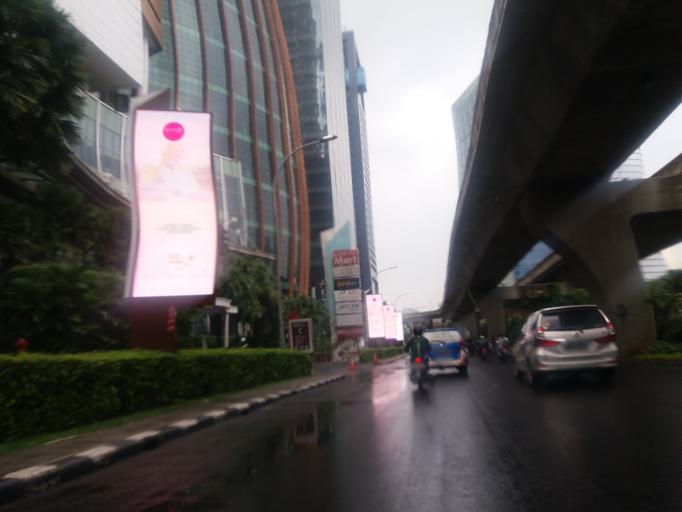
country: ID
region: Jakarta Raya
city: Jakarta
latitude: -6.2251
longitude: 106.8296
